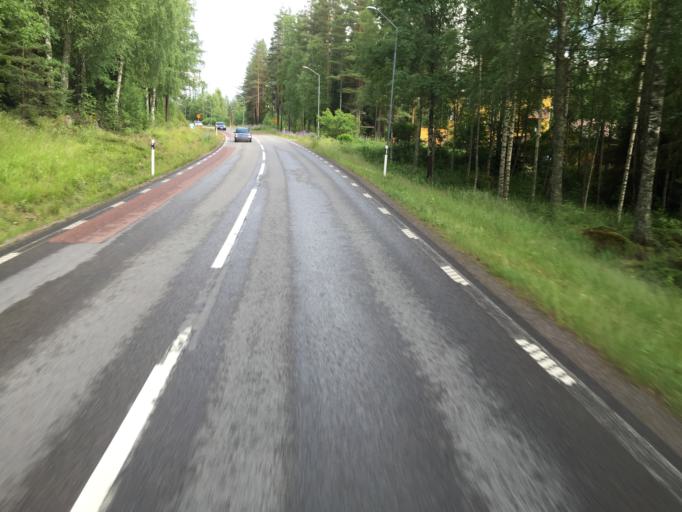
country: SE
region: Dalarna
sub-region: Vansbro Kommun
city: Vansbro
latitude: 60.5098
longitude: 14.2517
